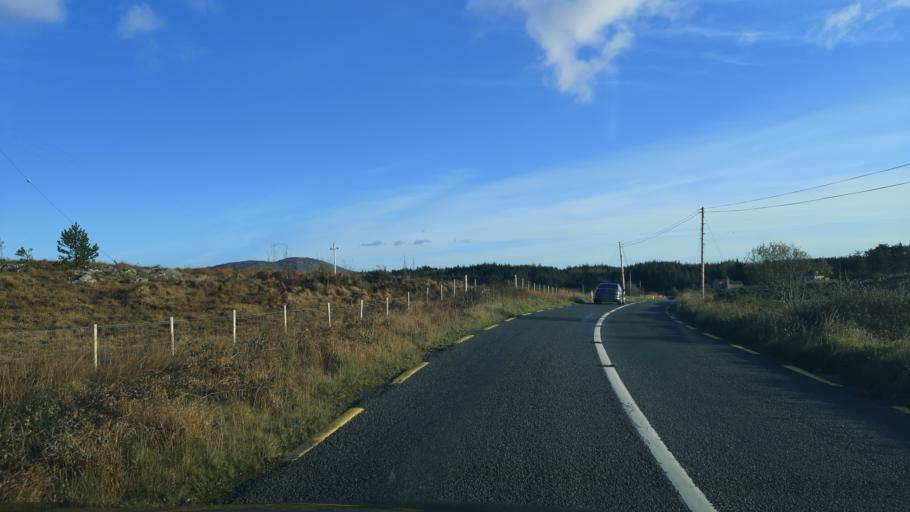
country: IE
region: Connaught
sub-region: County Galway
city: Clifden
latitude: 53.4628
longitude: -9.6899
